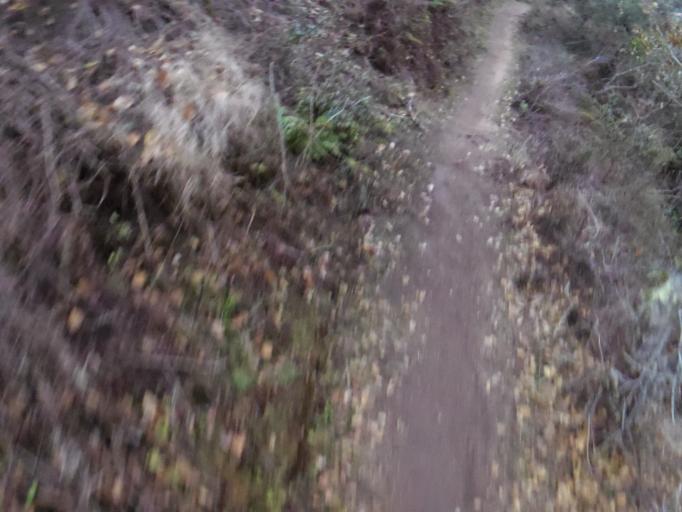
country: US
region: California
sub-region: Monterey County
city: Salinas
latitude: 36.5763
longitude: -121.6838
